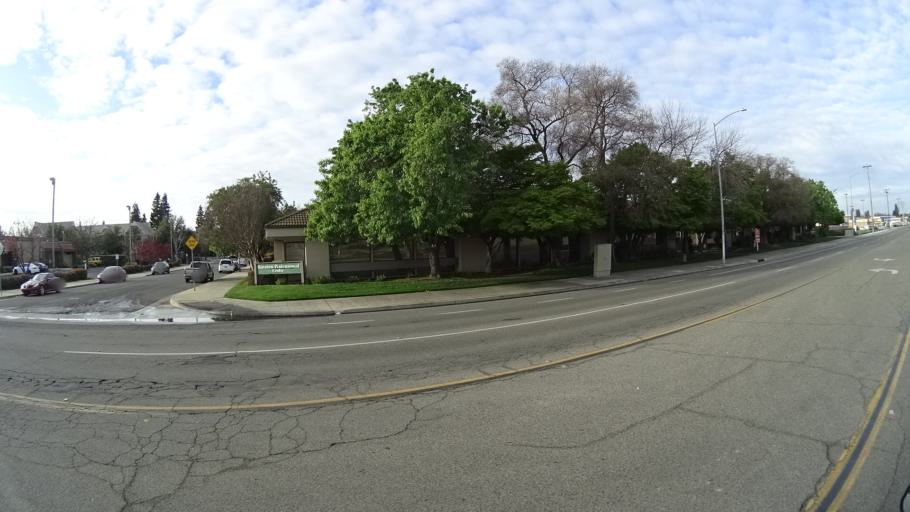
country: US
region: California
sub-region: Fresno County
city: Fresno
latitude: 36.8157
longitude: -119.7872
